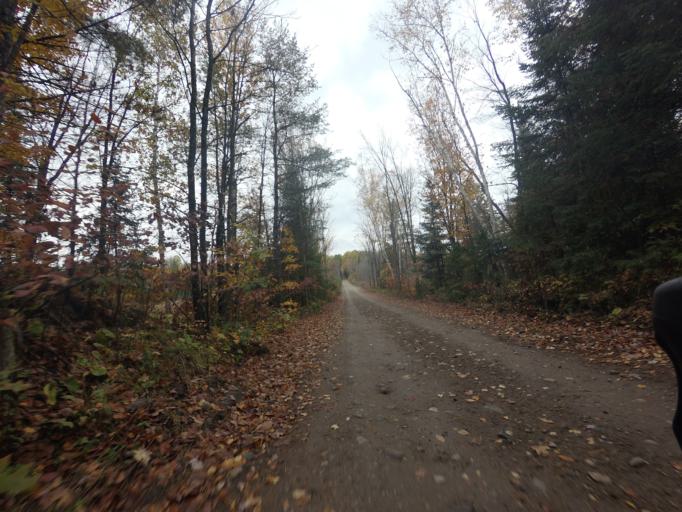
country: CA
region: Ontario
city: Renfrew
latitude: 45.1816
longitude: -76.6843
